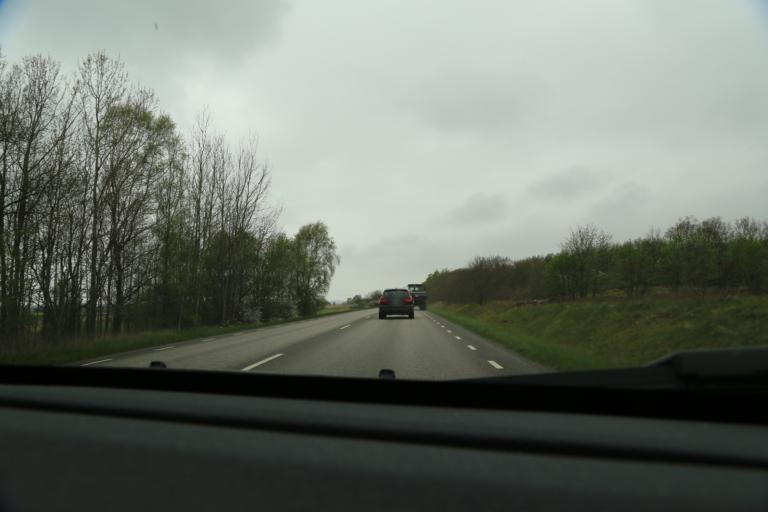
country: SE
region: Halland
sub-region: Kungsbacka Kommun
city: Frillesas
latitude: 57.2368
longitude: 12.1791
